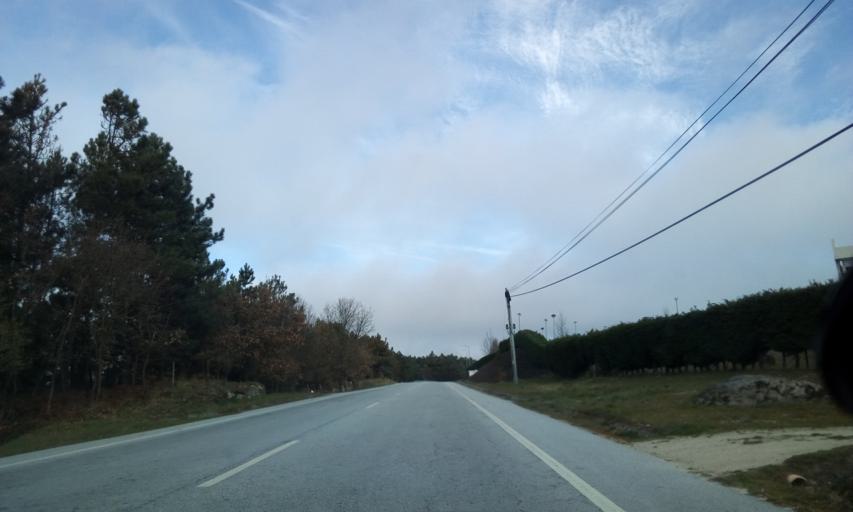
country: PT
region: Guarda
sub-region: Aguiar da Beira
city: Aguiar da Beira
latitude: 40.8116
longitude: -7.5347
